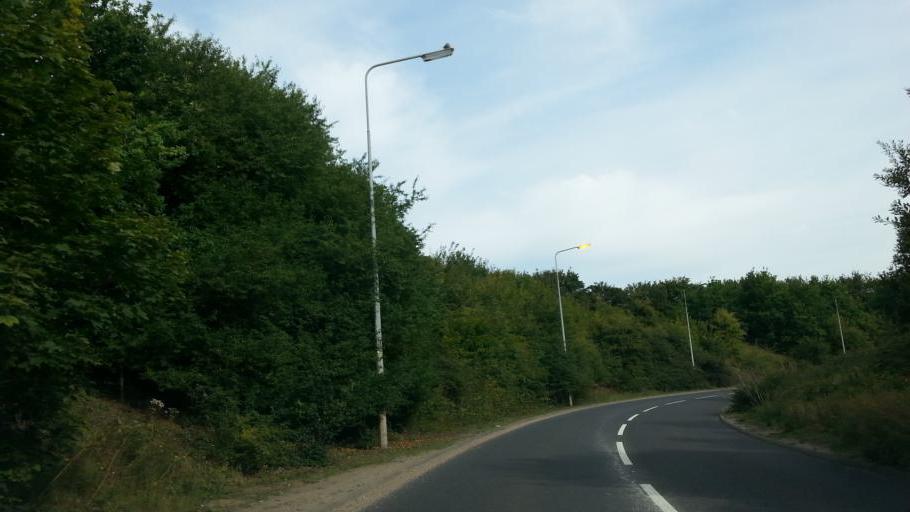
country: GB
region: England
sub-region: Suffolk
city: Bramford
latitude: 52.0634
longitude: 1.1052
